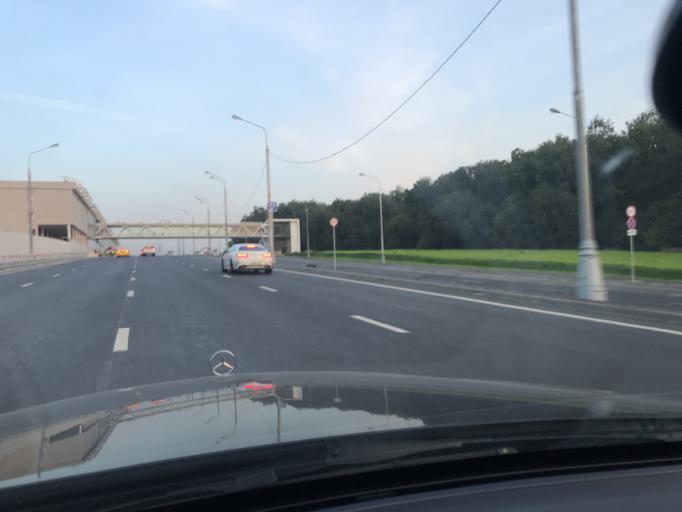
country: RU
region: Moskovskaya
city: Mosrentgen
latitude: 55.5874
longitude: 37.4303
